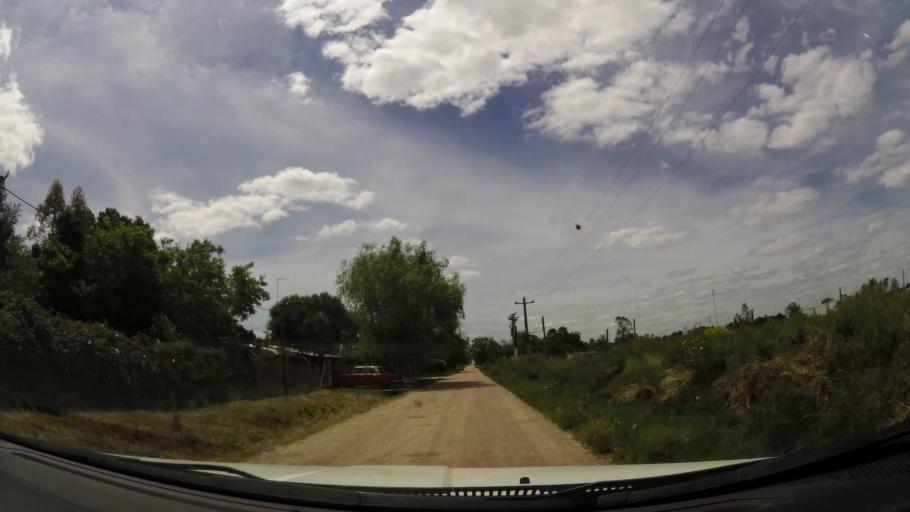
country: UY
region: San Jose
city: Delta del Tigre
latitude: -34.7528
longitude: -56.4127
